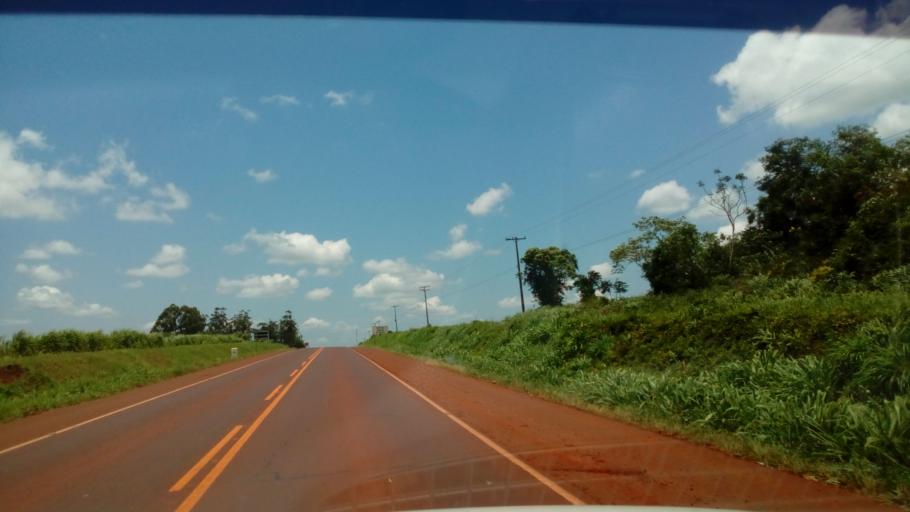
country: PY
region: Itapua
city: Arquitecto Tomas Romero Pereira
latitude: -26.3765
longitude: -55.2361
